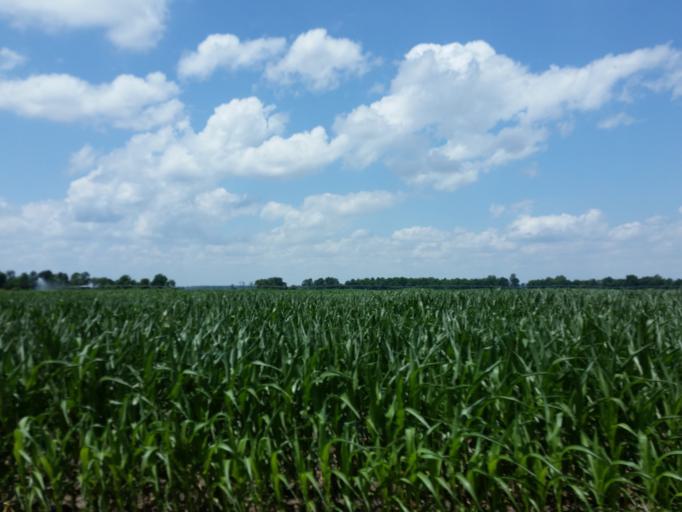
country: US
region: Kentucky
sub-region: Fulton County
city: Hickman
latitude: 36.5270
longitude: -89.3387
